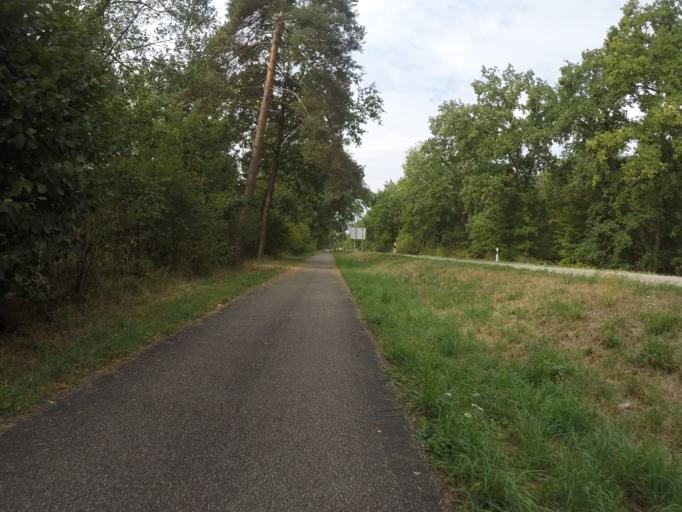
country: DE
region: Rheinland-Pfalz
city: Dudenhofen
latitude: 49.3469
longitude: 8.3777
